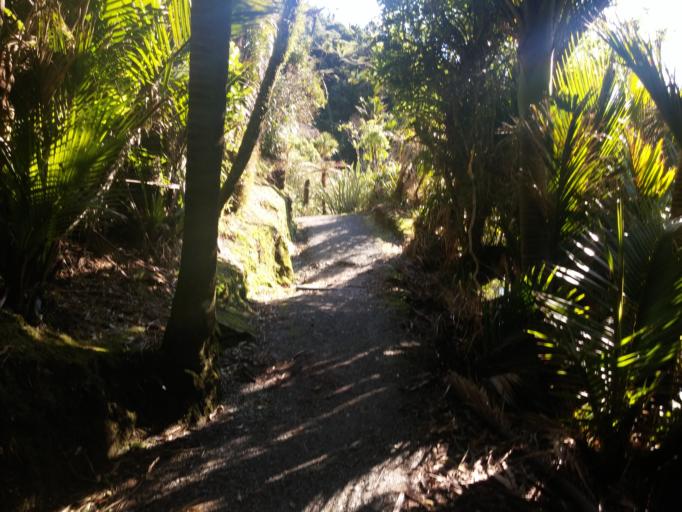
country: NZ
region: West Coast
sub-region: Grey District
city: Greymouth
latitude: -42.1095
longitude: 171.3426
